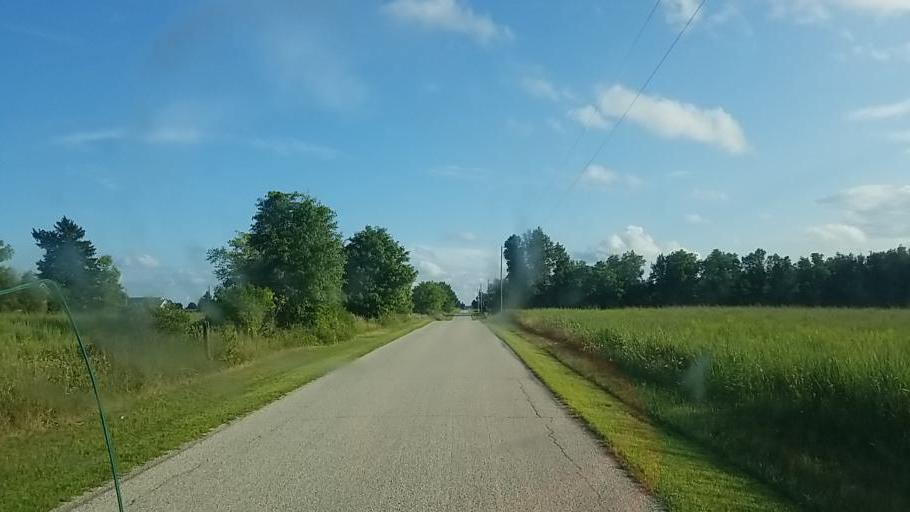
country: US
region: Ohio
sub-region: Crawford County
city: Bucyrus
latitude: 40.7647
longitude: -83.0550
